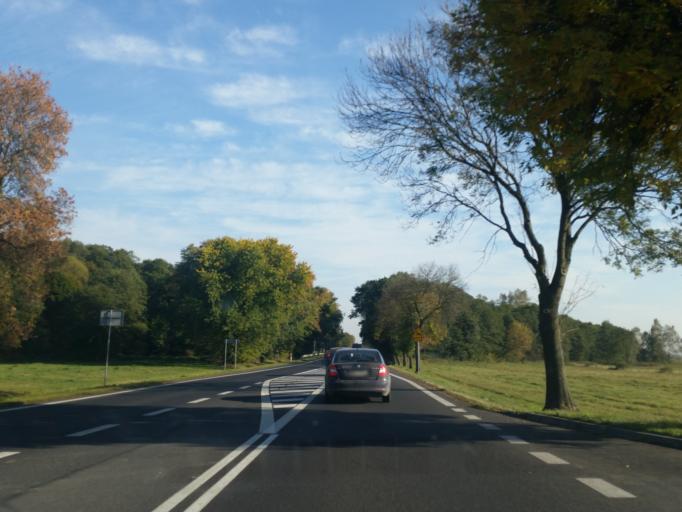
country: PL
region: Masovian Voivodeship
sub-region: Powiat sierpecki
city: Zawidz
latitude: 52.7795
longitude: 19.9063
